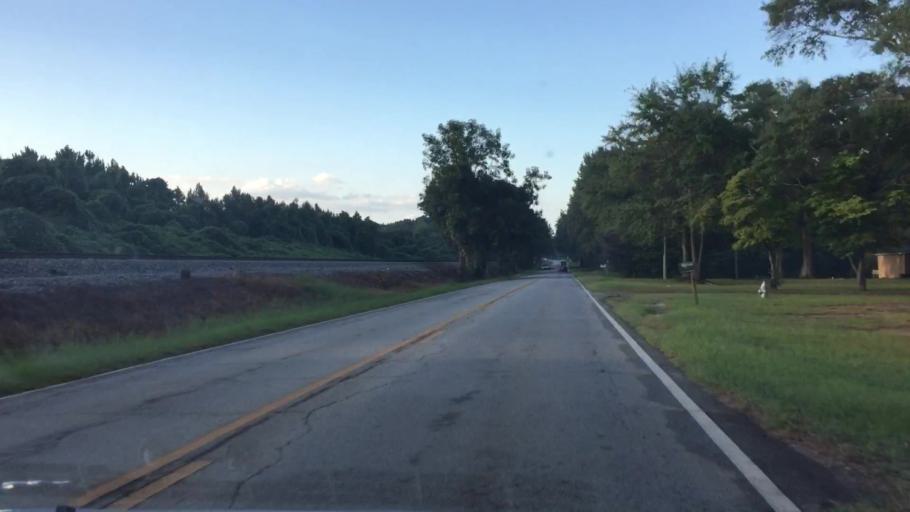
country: US
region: Georgia
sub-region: Henry County
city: Hampton
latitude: 33.4163
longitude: -84.2855
